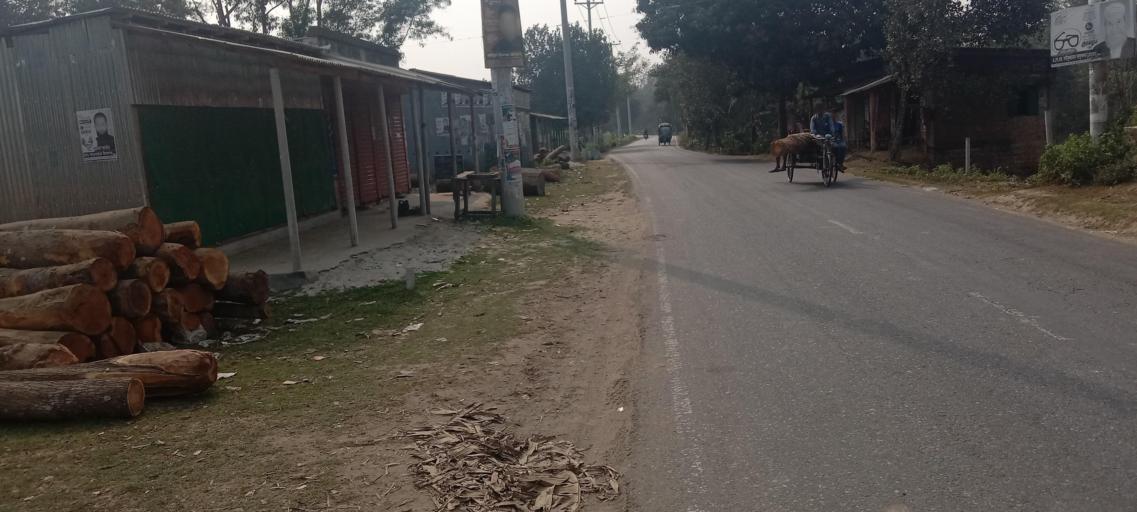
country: BD
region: Dhaka
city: Sakhipur
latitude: 24.4475
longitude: 90.3210
